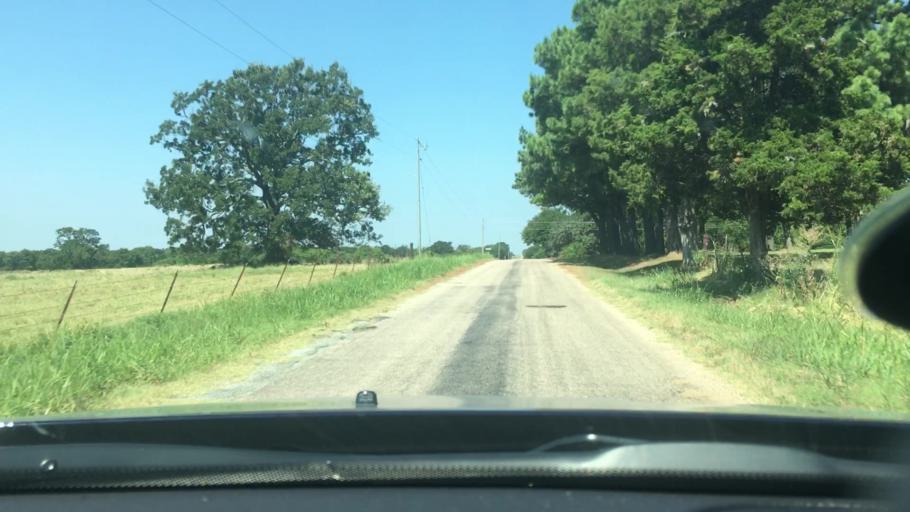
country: US
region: Oklahoma
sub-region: Johnston County
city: Tishomingo
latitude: 34.3176
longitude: -96.6432
